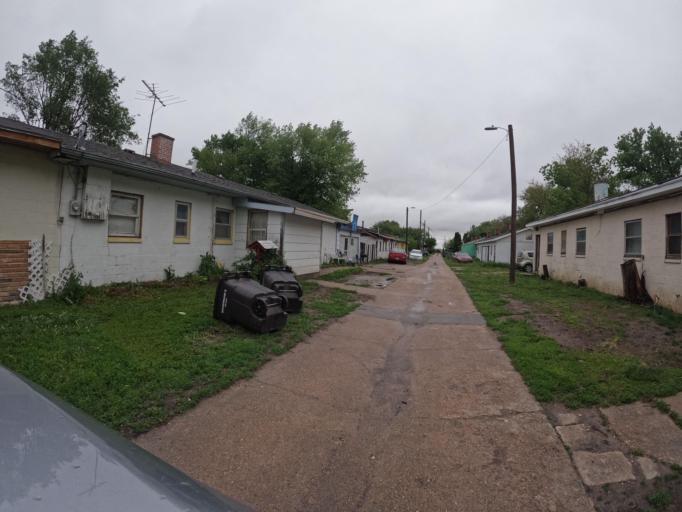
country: US
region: Nebraska
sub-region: Clay County
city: Harvard
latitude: 40.6277
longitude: -98.0927
